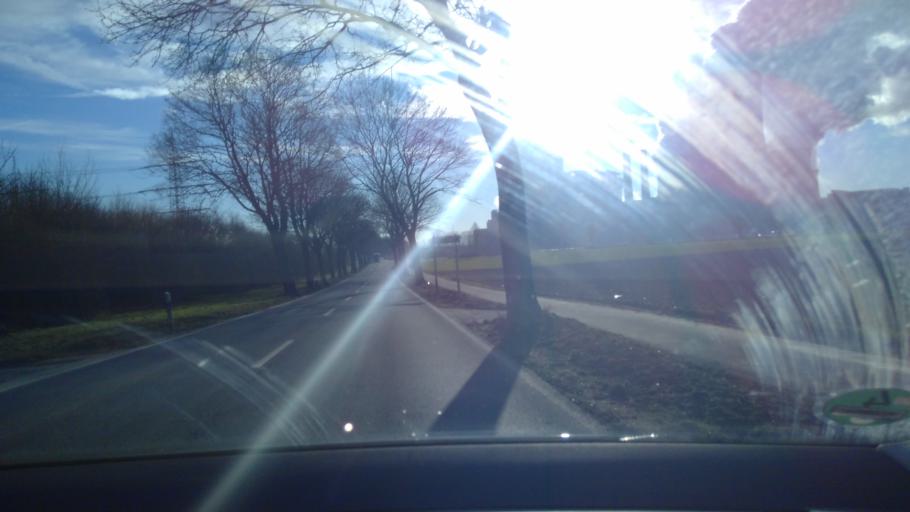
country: DE
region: North Rhine-Westphalia
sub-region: Regierungsbezirk Dusseldorf
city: Rommerskirchen
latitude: 51.0026
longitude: 6.6819
